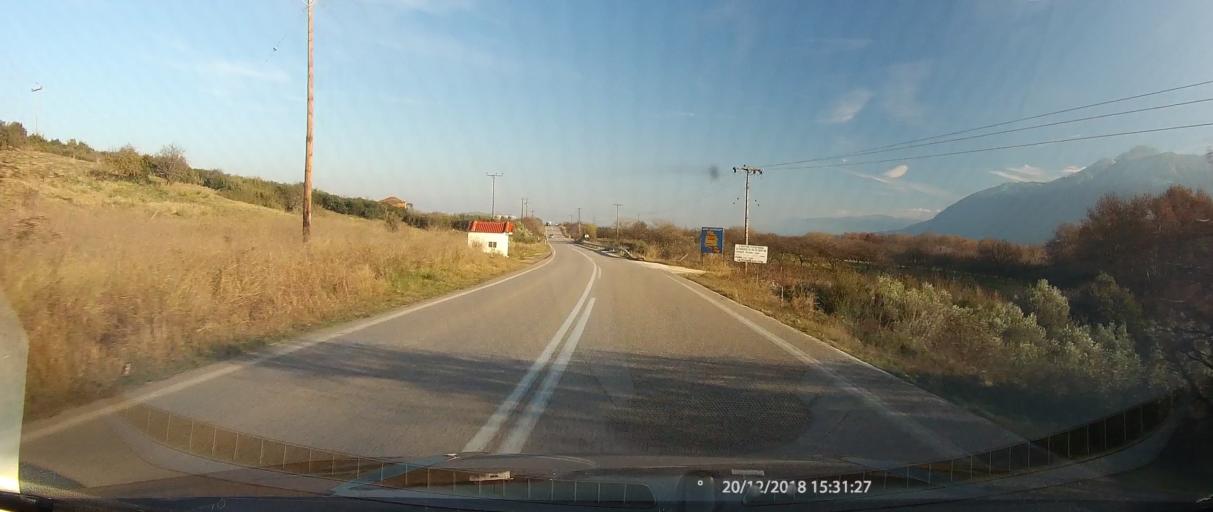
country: GR
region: Central Greece
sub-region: Nomos Fthiotidos
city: Lianokladhion
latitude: 38.9308
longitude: 22.2391
